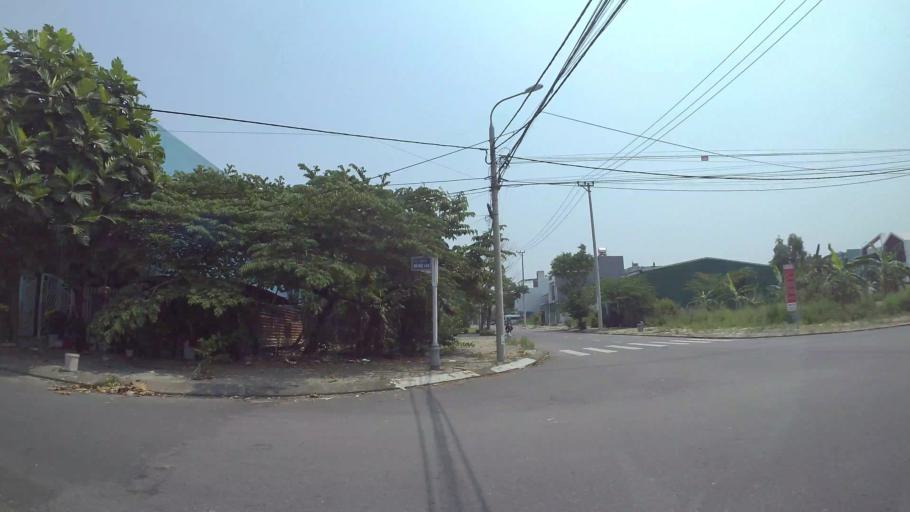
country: VN
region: Da Nang
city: Cam Le
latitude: 15.9923
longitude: 108.2109
